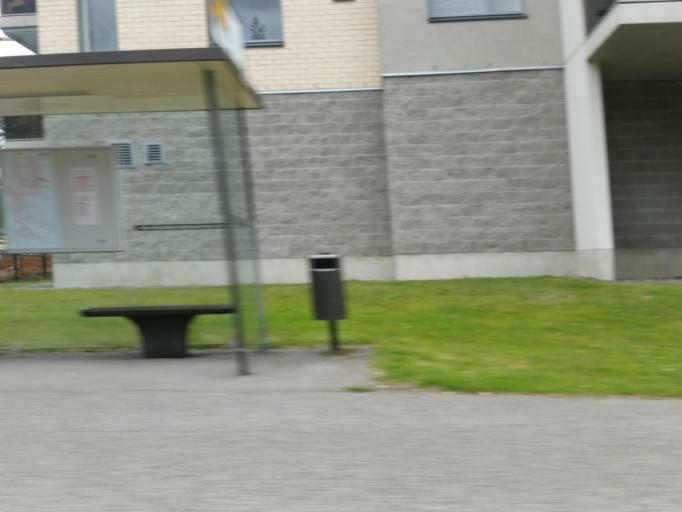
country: FI
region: Northern Savo
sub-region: Kuopio
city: Kuopio
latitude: 62.9031
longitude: 27.7058
